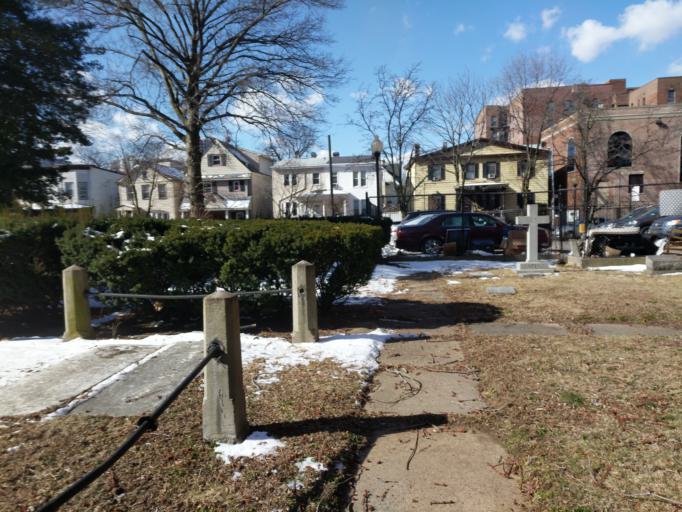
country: US
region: New York
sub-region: Queens County
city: Jamaica
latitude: 40.7042
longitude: -73.8017
